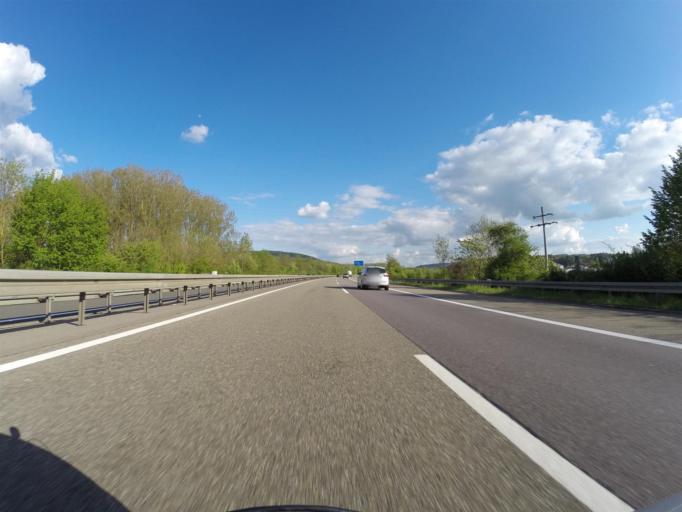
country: DE
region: Saarland
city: Merzig
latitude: 49.4477
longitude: 6.6207
